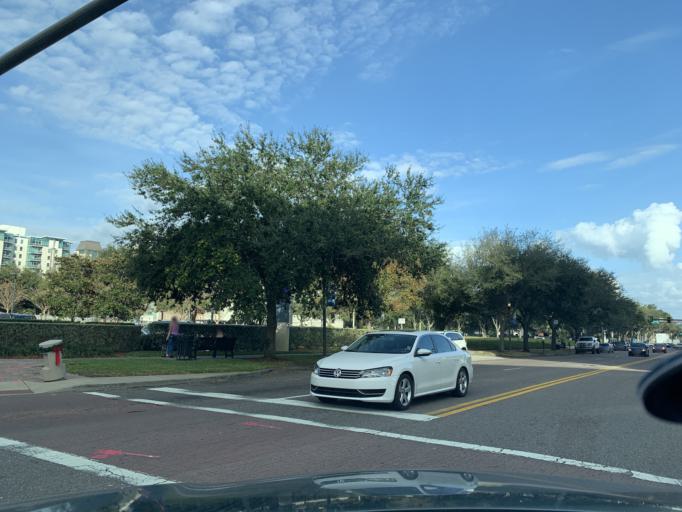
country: US
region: Florida
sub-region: Pinellas County
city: Saint Petersburg
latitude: 27.7642
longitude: -82.6400
